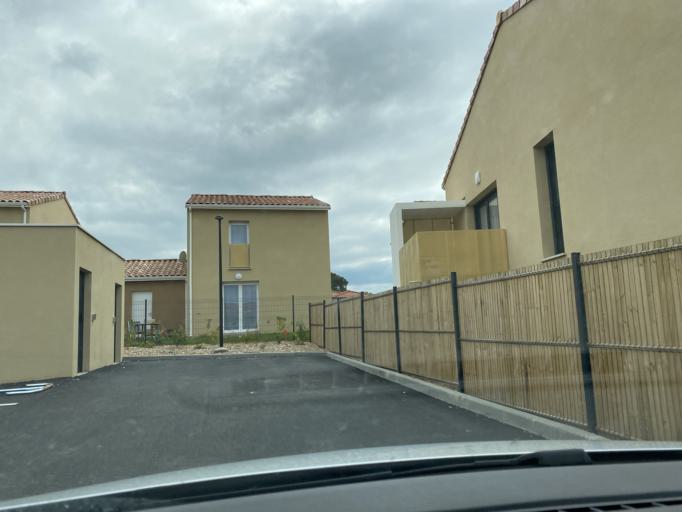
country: FR
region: Midi-Pyrenees
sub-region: Departement de la Haute-Garonne
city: Ayguesvives
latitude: 43.4286
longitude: 1.5943
